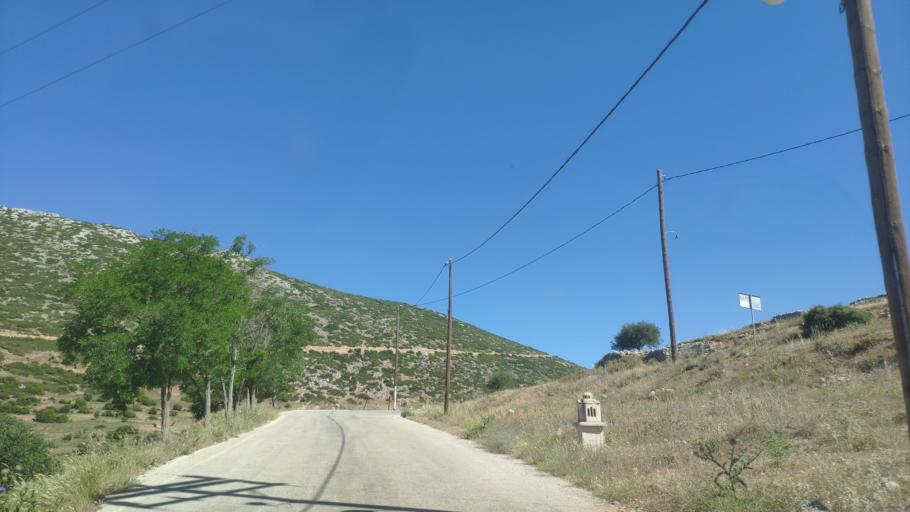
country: GR
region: Peloponnese
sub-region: Nomos Korinthias
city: Khiliomodhi
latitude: 37.7541
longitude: 22.8767
